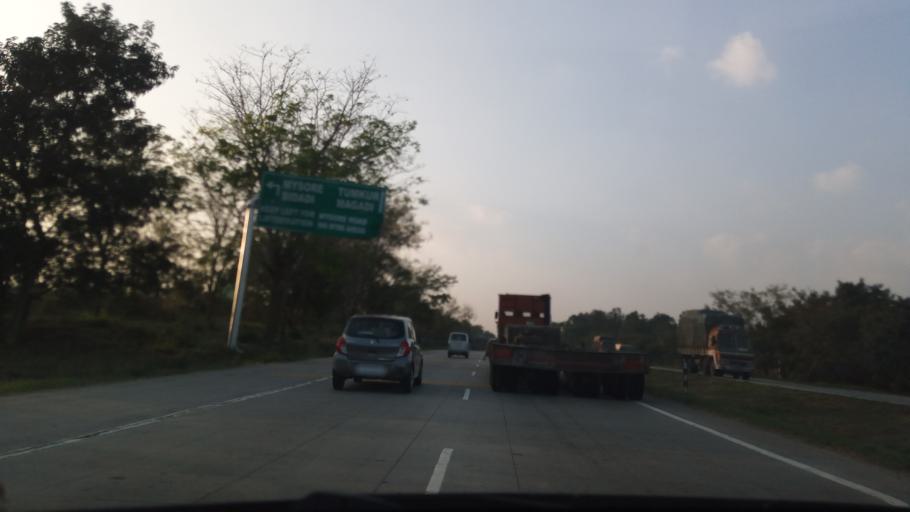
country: IN
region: Karnataka
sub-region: Bangalore Urban
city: Bangalore
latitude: 12.8961
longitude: 77.4756
